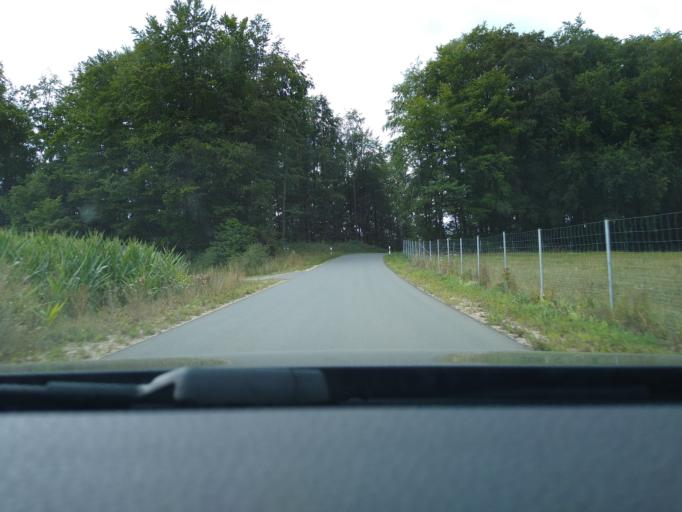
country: DE
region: Bavaria
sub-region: Upper Franconia
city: Obertrubach
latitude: 49.7075
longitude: 11.3871
